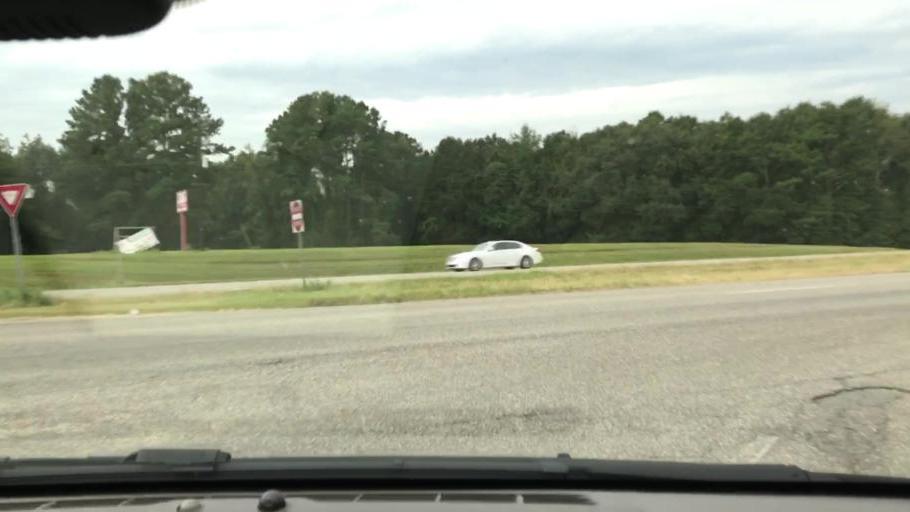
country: US
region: Alabama
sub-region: Houston County
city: Ashford
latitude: 31.1760
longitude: -85.2389
